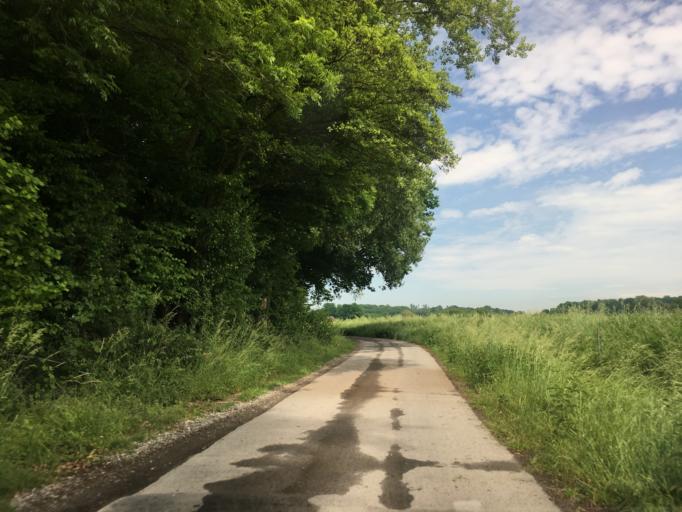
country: DE
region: North Rhine-Westphalia
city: Ludinghausen
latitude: 51.7730
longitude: 7.4885
